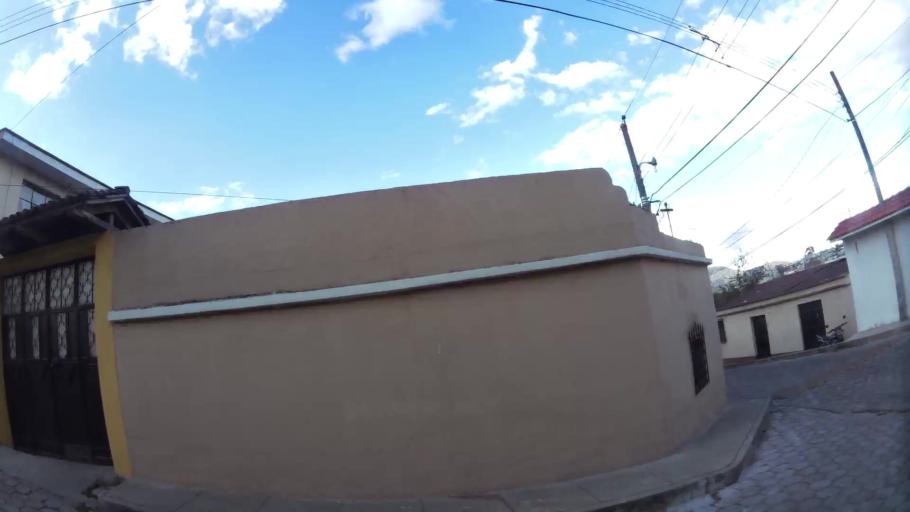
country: GT
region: Quetzaltenango
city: Quetzaltenango
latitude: 14.8533
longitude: -91.5262
